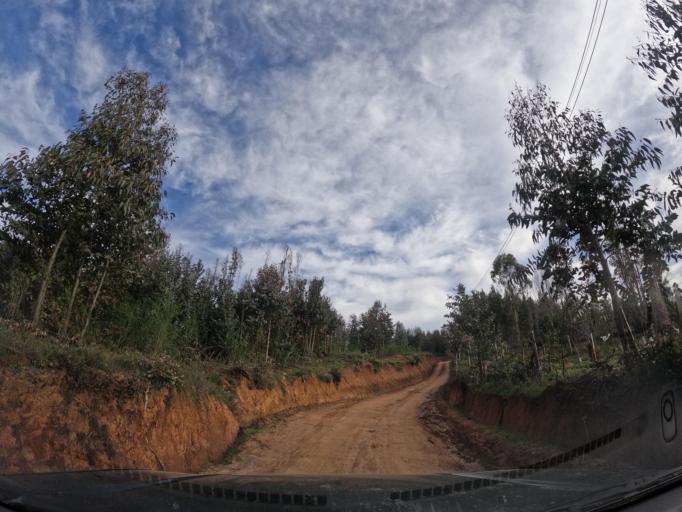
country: CL
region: Biobio
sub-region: Provincia de Concepcion
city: Chiguayante
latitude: -37.0351
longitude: -72.9047
